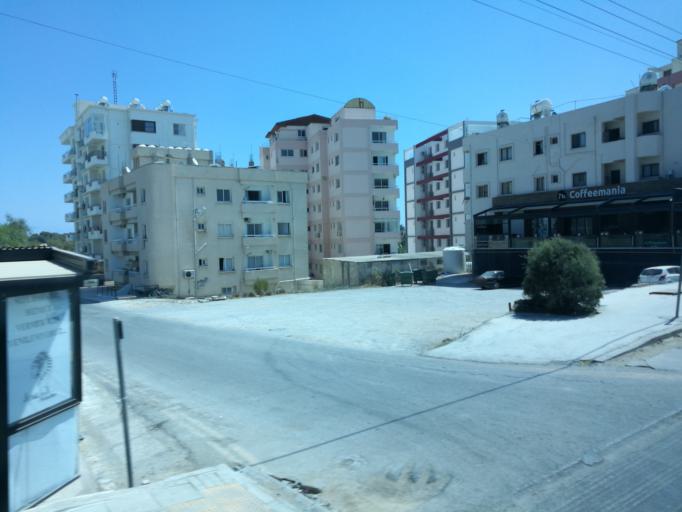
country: CY
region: Ammochostos
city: Famagusta
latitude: 35.1374
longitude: 33.9198
